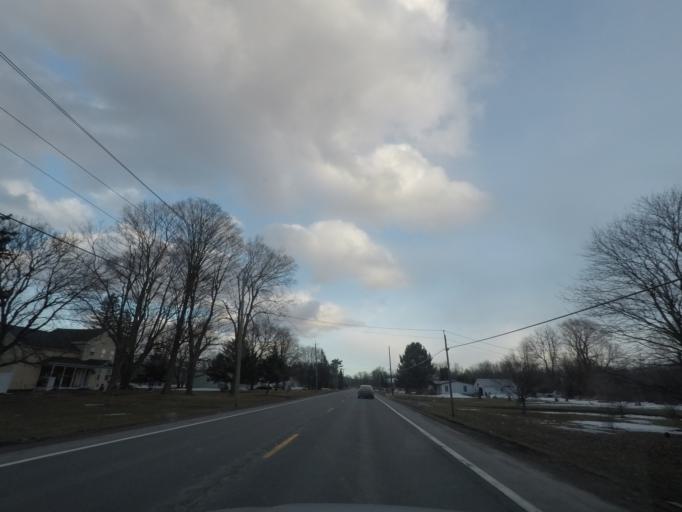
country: US
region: New York
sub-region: Herkimer County
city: Frankfort
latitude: 43.0700
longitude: -75.1030
